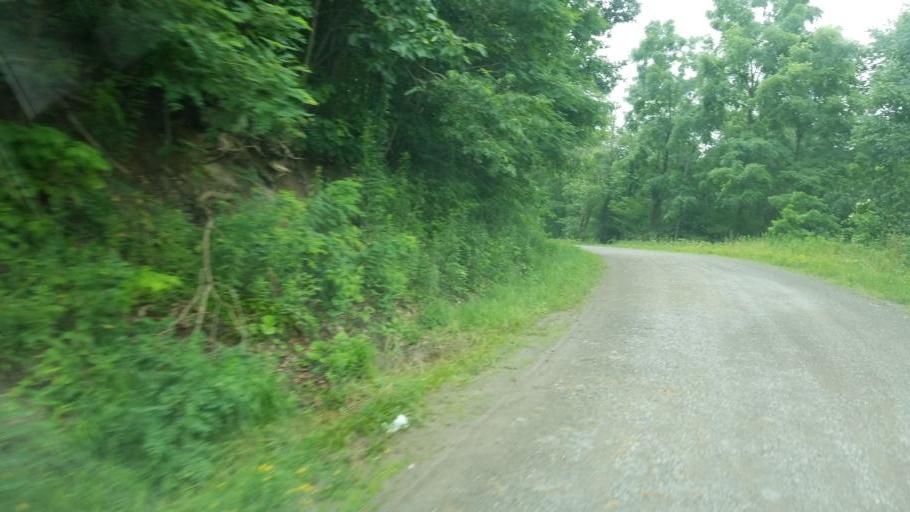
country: US
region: Ohio
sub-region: Columbiana County
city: Salineville
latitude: 40.5621
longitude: -80.8248
